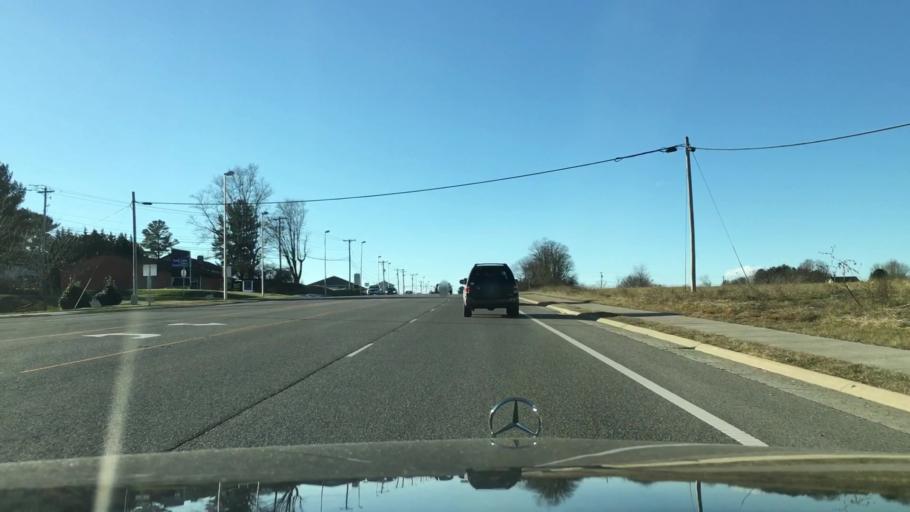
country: US
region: Virginia
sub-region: Montgomery County
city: Merrimac
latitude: 37.1624
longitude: -80.4325
